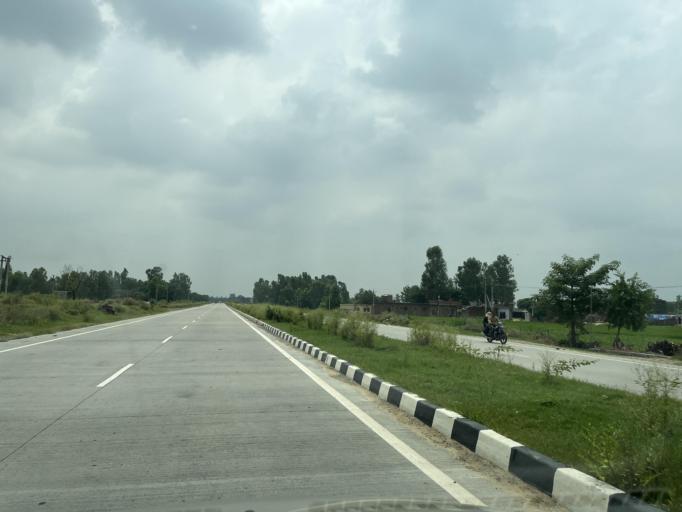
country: IN
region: Uttar Pradesh
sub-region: Bijnor
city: Najibabad
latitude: 29.5582
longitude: 78.3390
